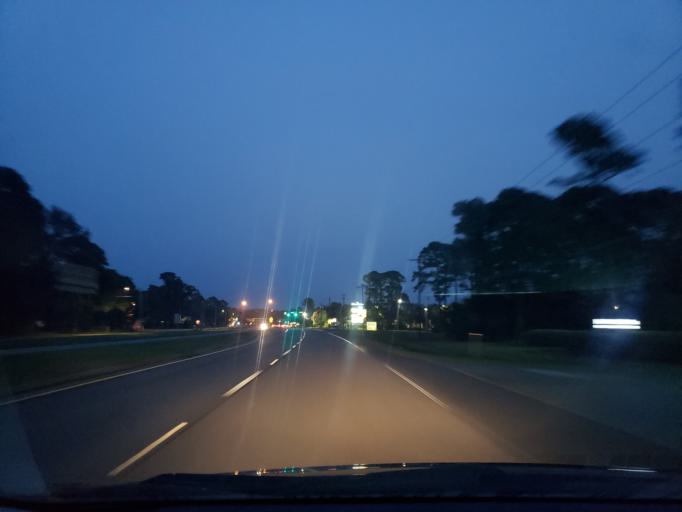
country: US
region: Georgia
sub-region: Chatham County
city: Whitemarsh Island
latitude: 32.0429
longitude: -81.0122
